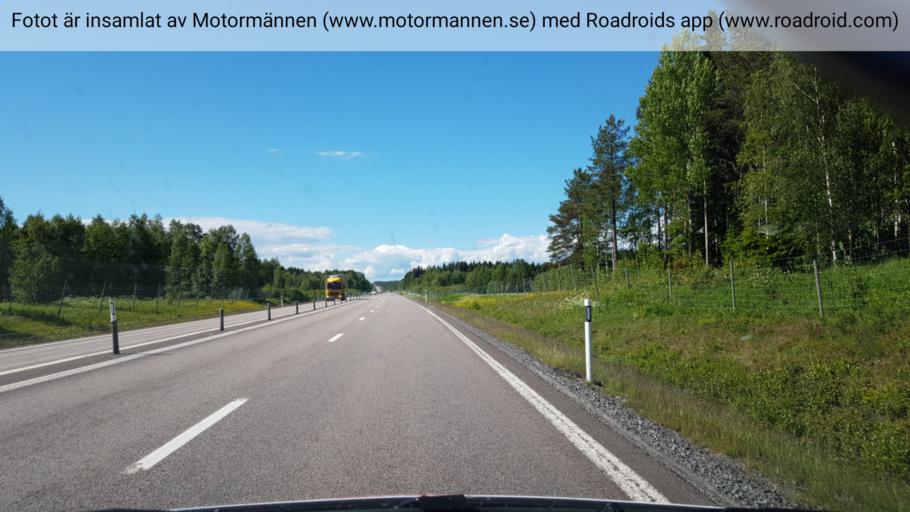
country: SE
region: Norrbotten
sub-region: Kalix Kommun
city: Rolfs
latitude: 65.8897
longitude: 22.9138
